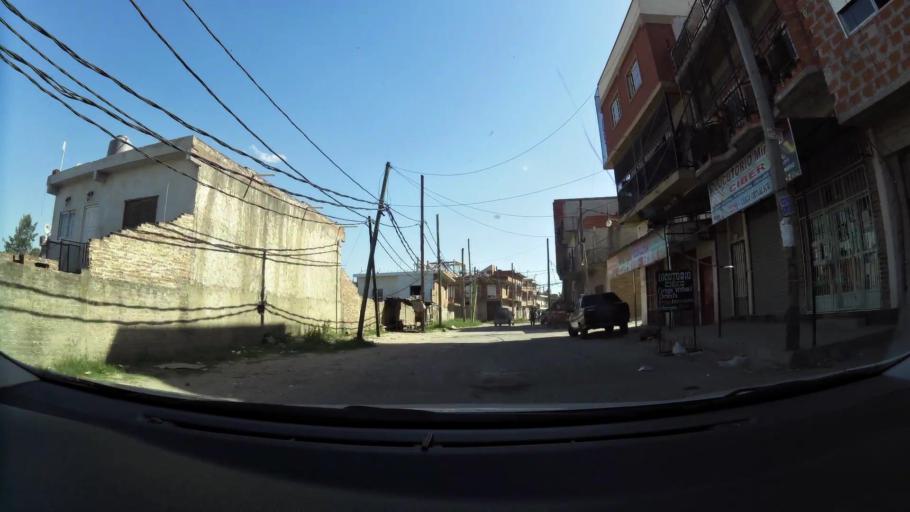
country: AR
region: Buenos Aires F.D.
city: Villa Lugano
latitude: -34.7075
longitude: -58.4820
